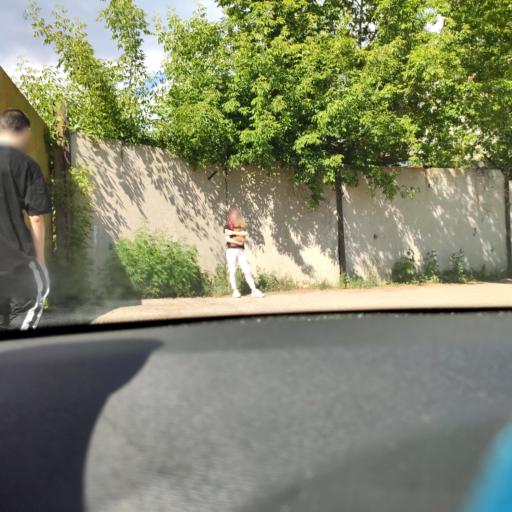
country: RU
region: Samara
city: Rozhdestveno
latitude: 53.1610
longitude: 50.0729
